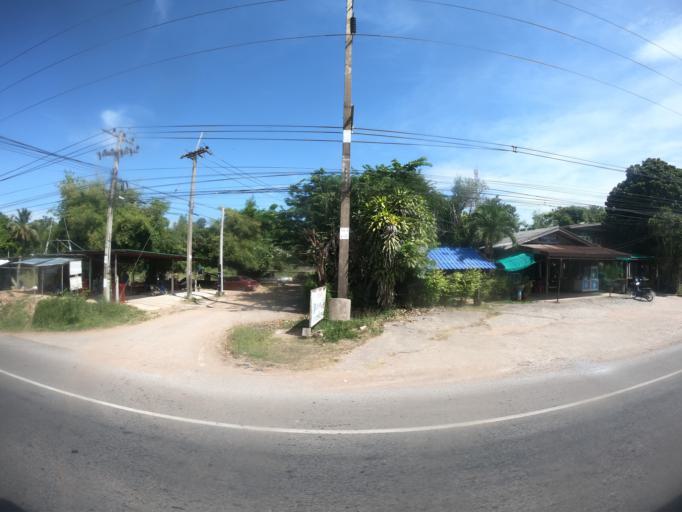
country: TH
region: Khon Kaen
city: Khon Kaen
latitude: 16.4454
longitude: 102.9618
